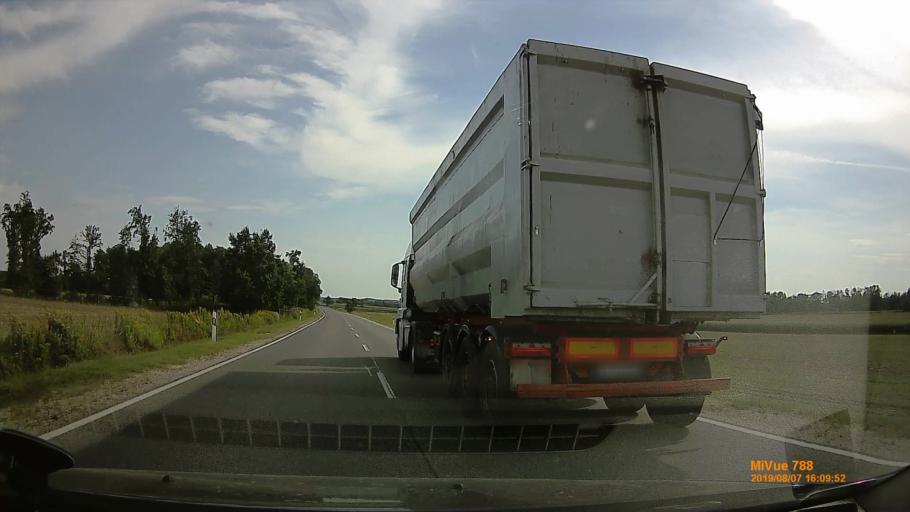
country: HU
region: Zala
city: Zalalovo
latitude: 46.8874
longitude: 16.6005
